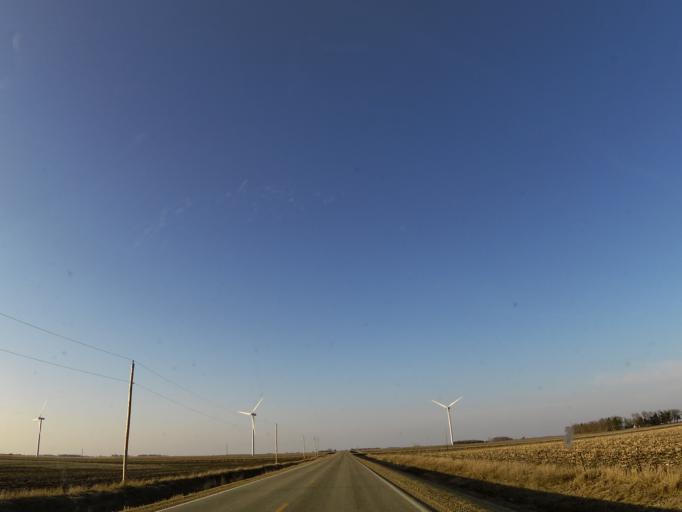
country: US
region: Iowa
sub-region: Worth County
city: Northwood
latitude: 43.4128
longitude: -93.1243
